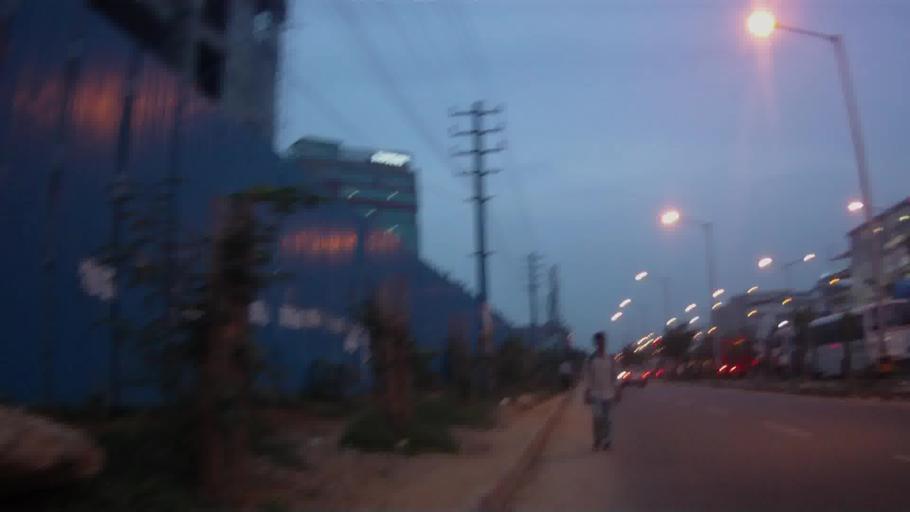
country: IN
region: Karnataka
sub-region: Bangalore Urban
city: Bangalore
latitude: 12.9809
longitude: 77.6942
